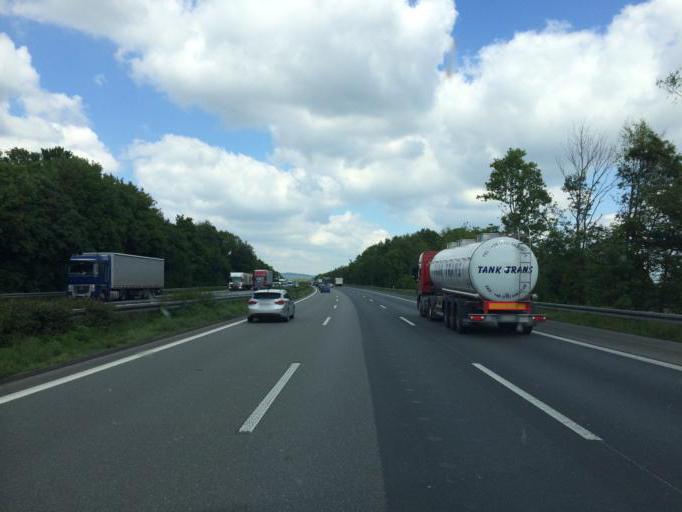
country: DE
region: North Rhine-Westphalia
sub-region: Regierungsbezirk Detmold
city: Verl
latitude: 51.9097
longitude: 8.5105
